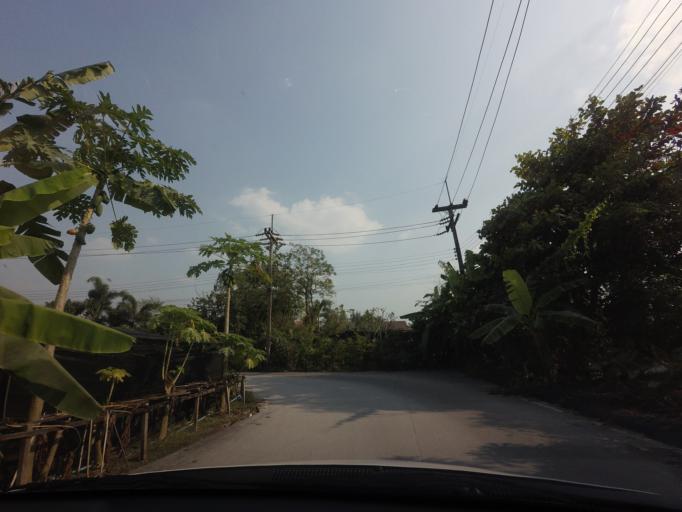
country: TH
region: Samut Sakhon
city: Krathum Baen
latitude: 13.6905
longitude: 100.2537
